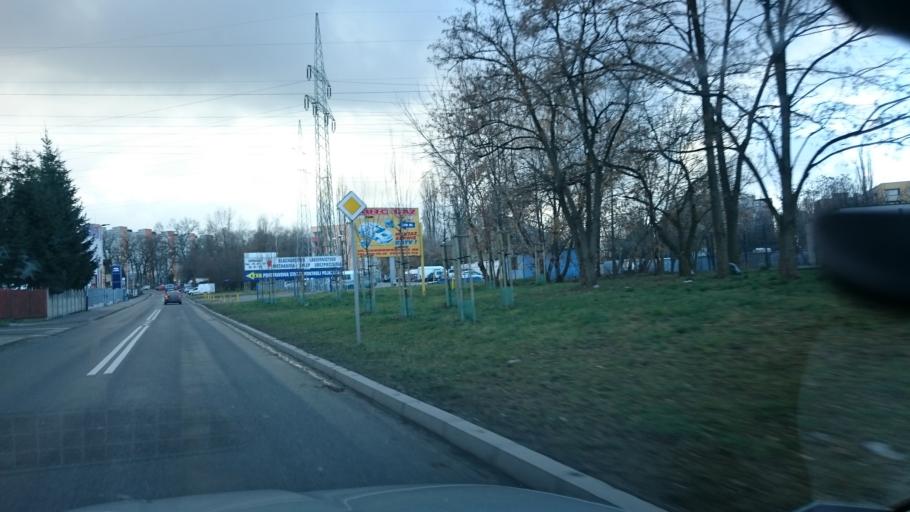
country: PL
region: Lesser Poland Voivodeship
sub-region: Powiat wielicki
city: Czarnochowice
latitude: 50.0121
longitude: 20.0258
